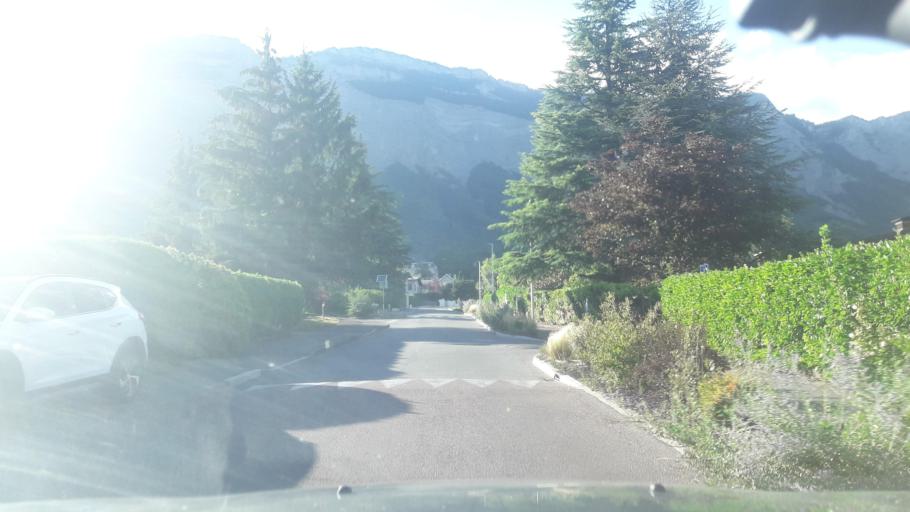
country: FR
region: Rhone-Alpes
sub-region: Departement de l'Isere
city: Biviers
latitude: 45.2339
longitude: 5.8061
